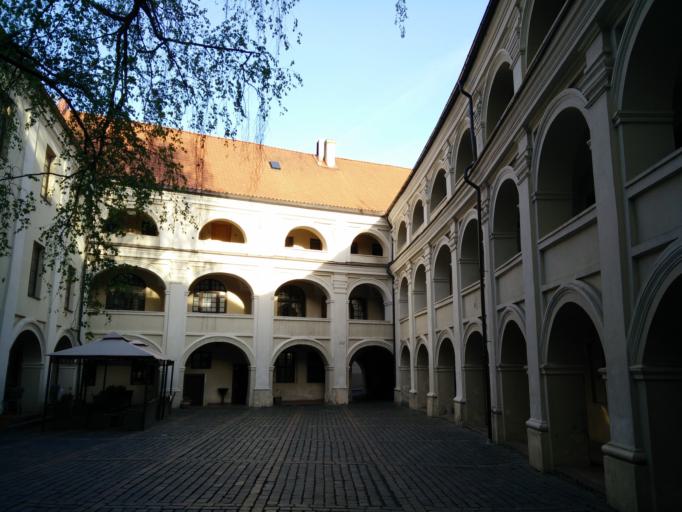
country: LT
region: Vilnius County
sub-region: Vilnius
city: Vilnius
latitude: 54.6823
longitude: 25.2858
